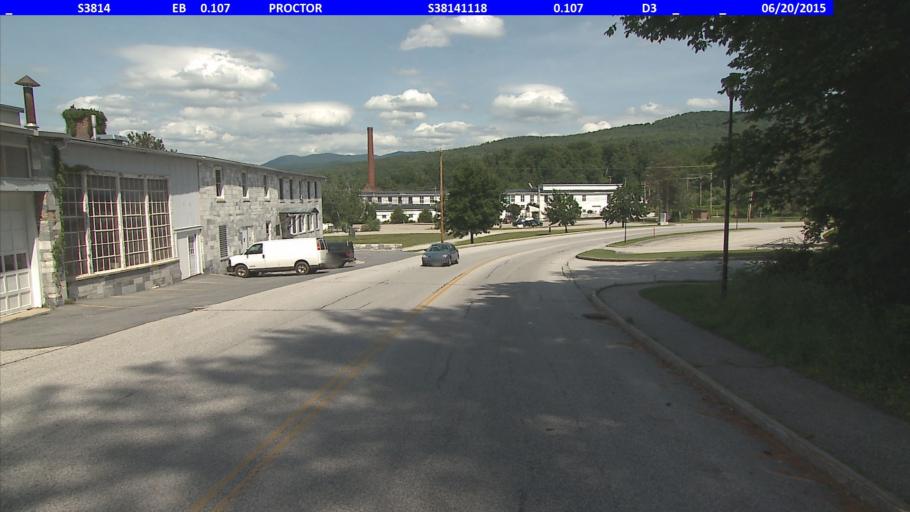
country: US
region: Vermont
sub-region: Rutland County
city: West Rutland
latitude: 43.6630
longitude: -73.0377
